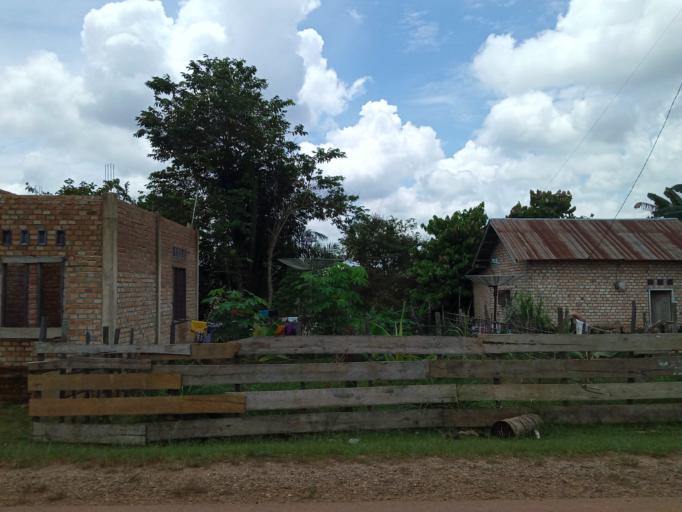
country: ID
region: Jambi
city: Mersam
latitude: -1.6466
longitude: 102.9705
